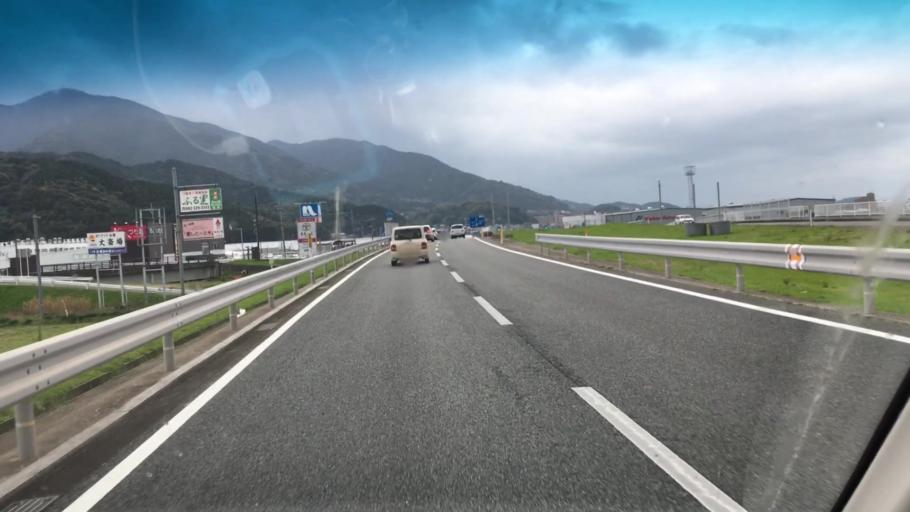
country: JP
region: Fukuoka
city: Maebaru-chuo
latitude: 33.5181
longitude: 130.1573
